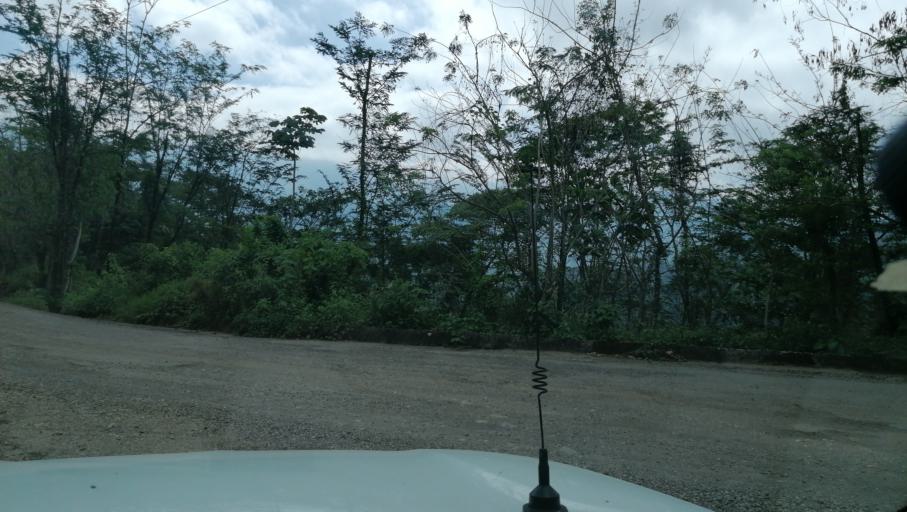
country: MX
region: Chiapas
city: Ixtacomitan
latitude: 17.3576
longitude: -93.1161
